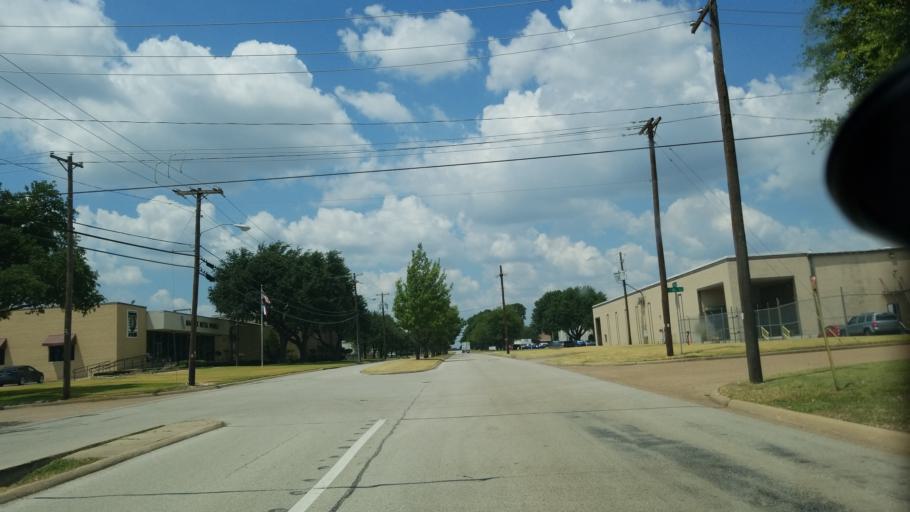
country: US
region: Texas
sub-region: Dallas County
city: Duncanville
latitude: 32.6873
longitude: -96.8861
